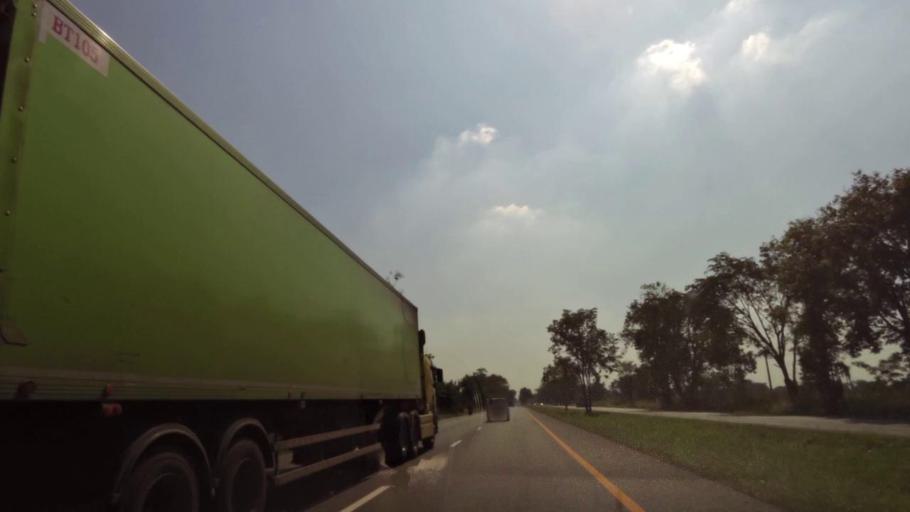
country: TH
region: Phichit
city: Bueng Na Rang
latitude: 16.2274
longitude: 100.1260
